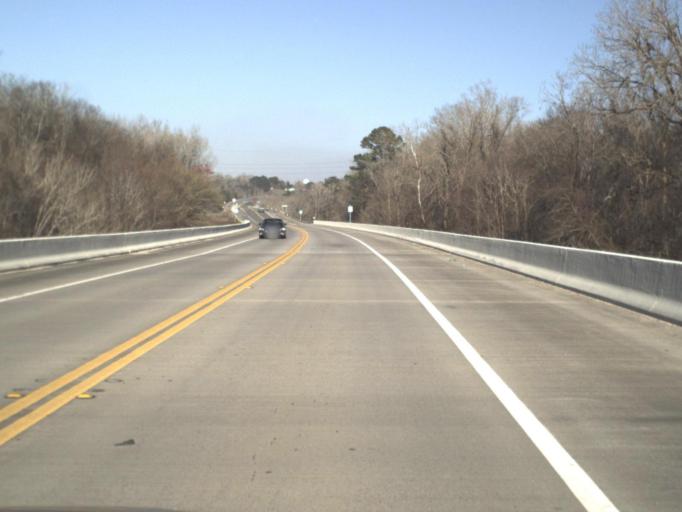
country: US
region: Florida
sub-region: Gadsden County
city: Chattahoochee
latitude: 30.6988
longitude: -84.8642
